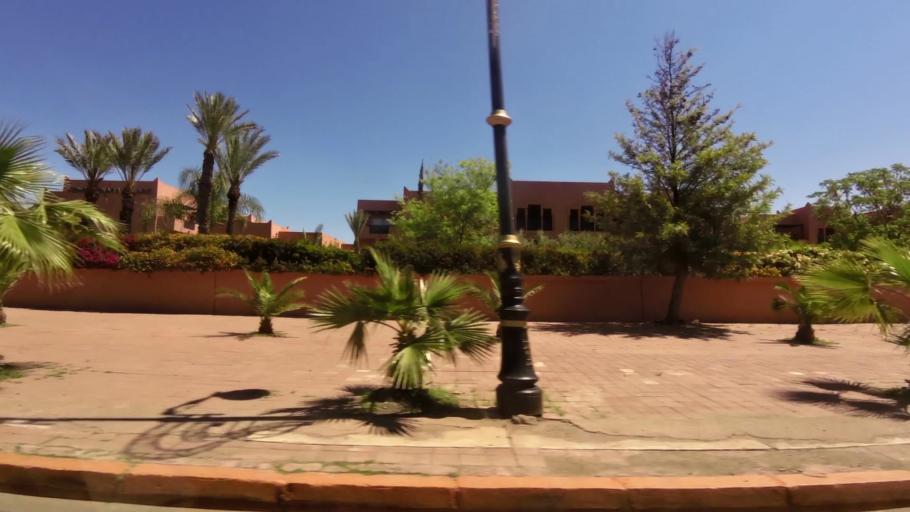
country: MA
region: Marrakech-Tensift-Al Haouz
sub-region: Marrakech
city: Marrakesh
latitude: 31.5874
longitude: -7.9879
